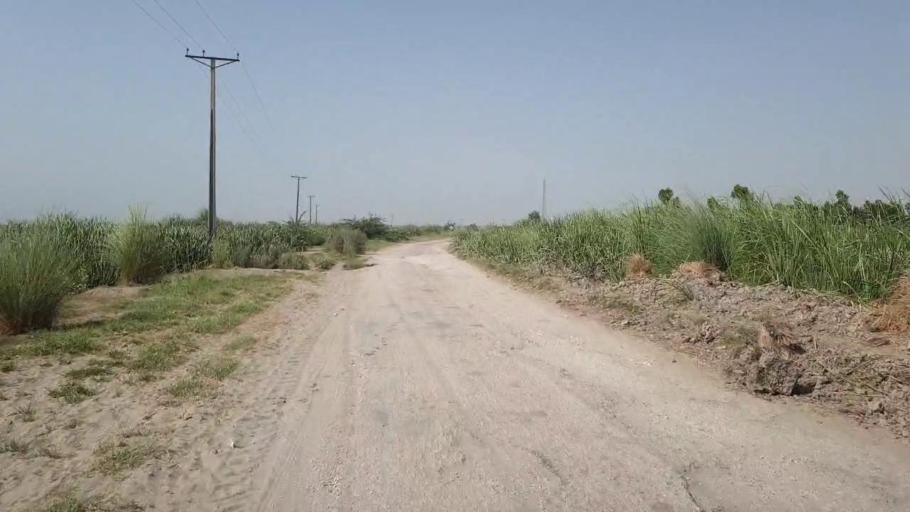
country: PK
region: Sindh
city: Jam Sahib
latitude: 26.4239
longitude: 68.9082
